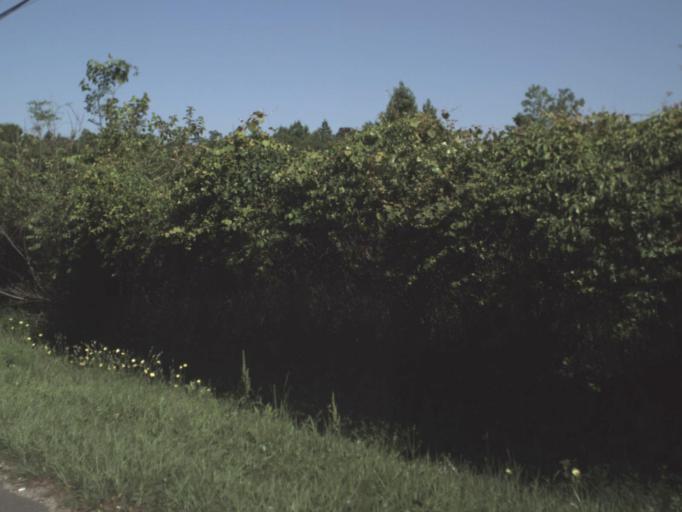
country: US
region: Florida
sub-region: Duval County
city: Jacksonville
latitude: 30.3251
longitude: -81.7460
